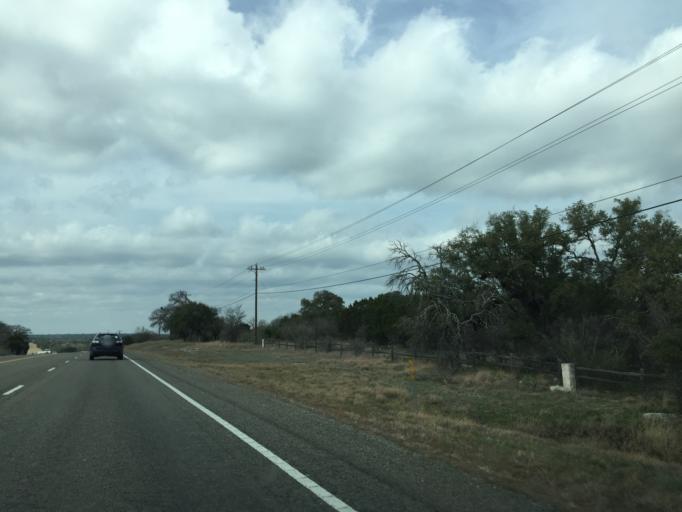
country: US
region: Texas
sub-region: Burnet County
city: Meadowlakes
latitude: 30.4922
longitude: -98.2337
